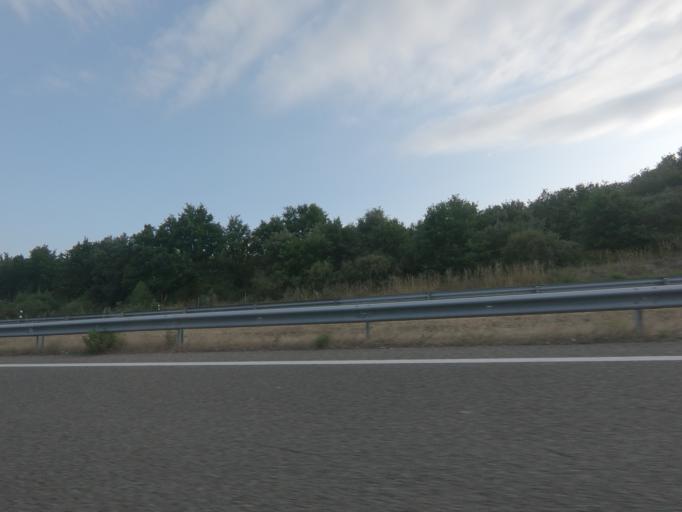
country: ES
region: Galicia
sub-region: Provincia de Ourense
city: Allariz
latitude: 42.1991
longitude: -7.7827
